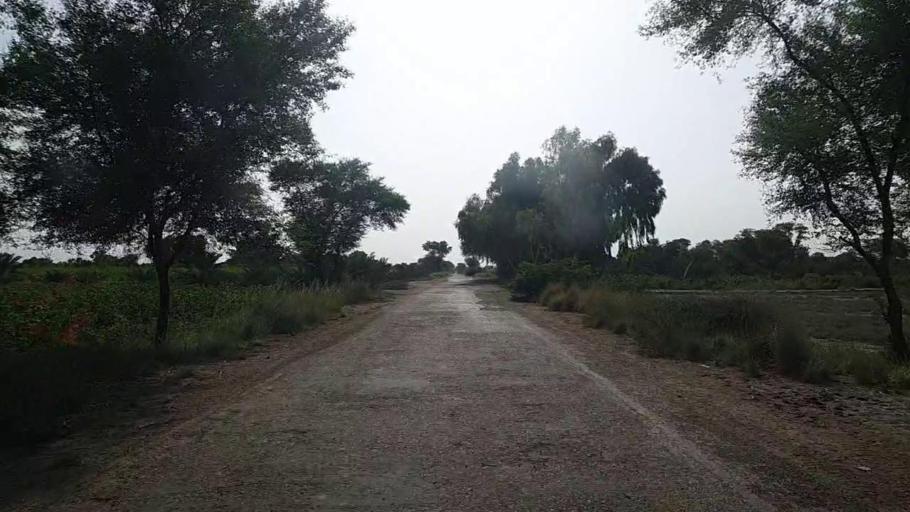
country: PK
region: Sindh
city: Pad Idan
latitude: 26.8532
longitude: 68.3274
